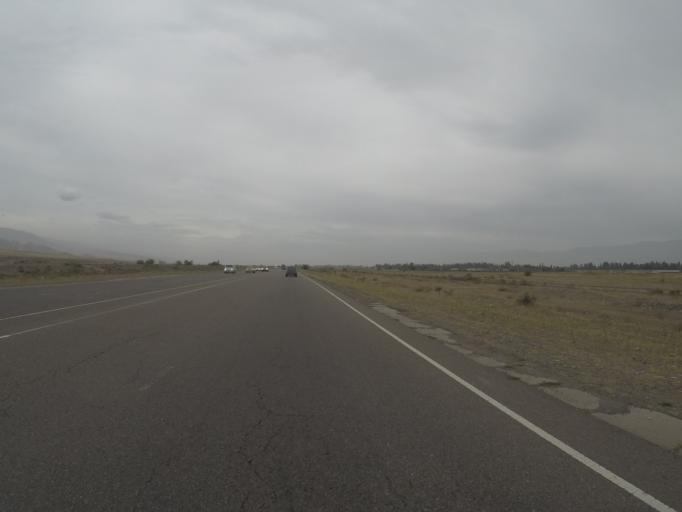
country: KG
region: Chuy
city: Bystrovka
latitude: 42.8299
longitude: 75.5189
